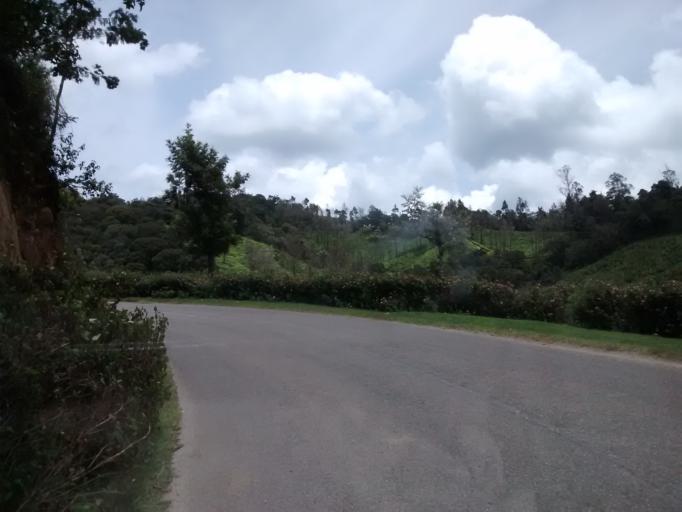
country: IN
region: Kerala
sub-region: Idukki
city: Munnar
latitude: 10.1262
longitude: 77.2180
